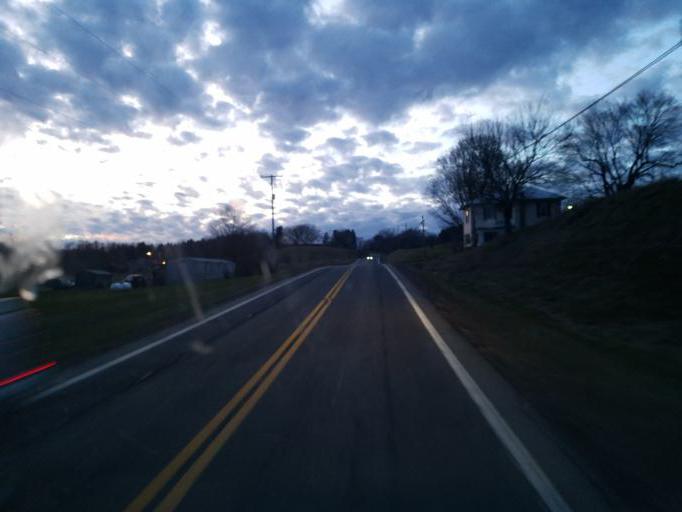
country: US
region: Ohio
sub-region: Knox County
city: Gambier
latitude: 40.2807
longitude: -82.3065
